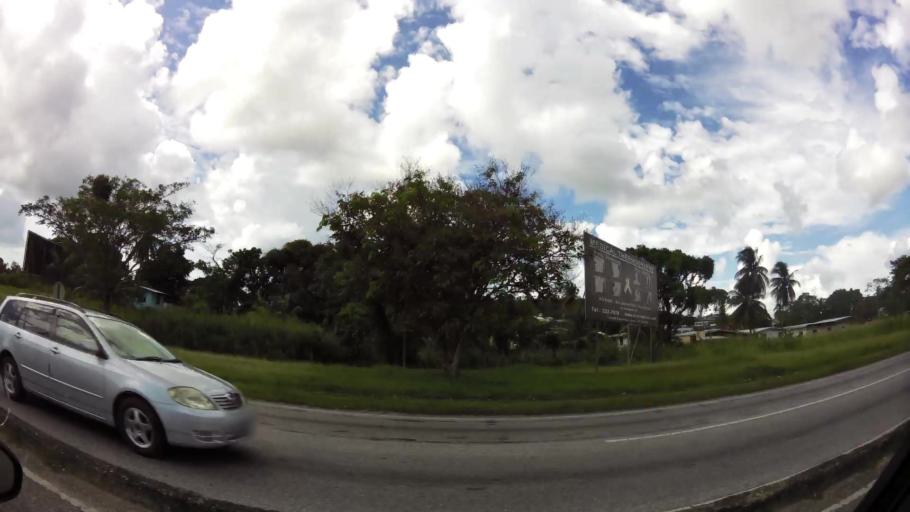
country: TT
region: City of San Fernando
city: Mon Repos
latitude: 10.2741
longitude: -61.4519
